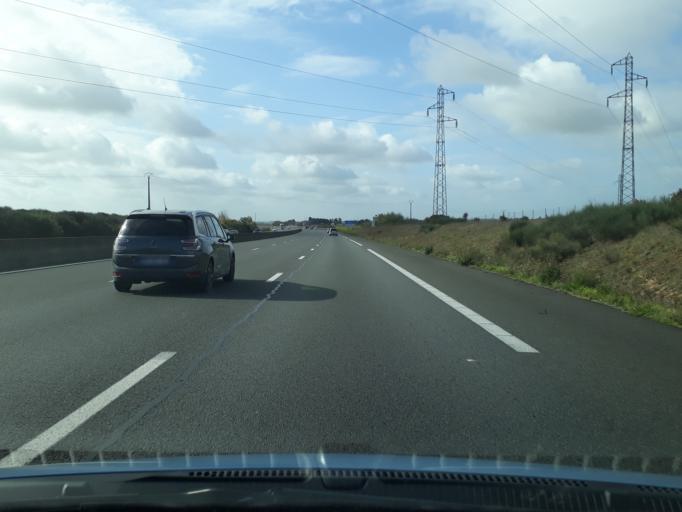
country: FR
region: Centre
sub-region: Departement du Loir-et-Cher
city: Montlivault
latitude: 47.6732
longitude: 1.3966
